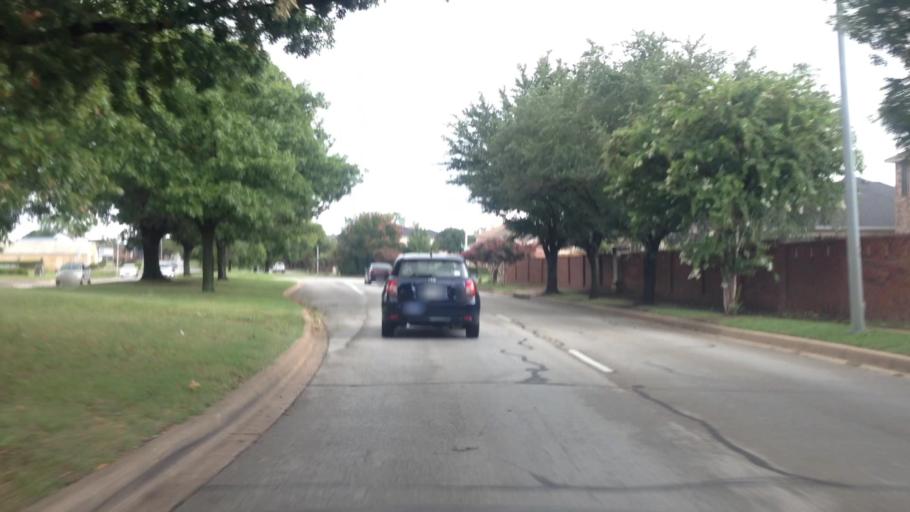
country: US
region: Texas
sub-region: Tarrant County
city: Edgecliff Village
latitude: 32.6384
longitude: -97.3954
